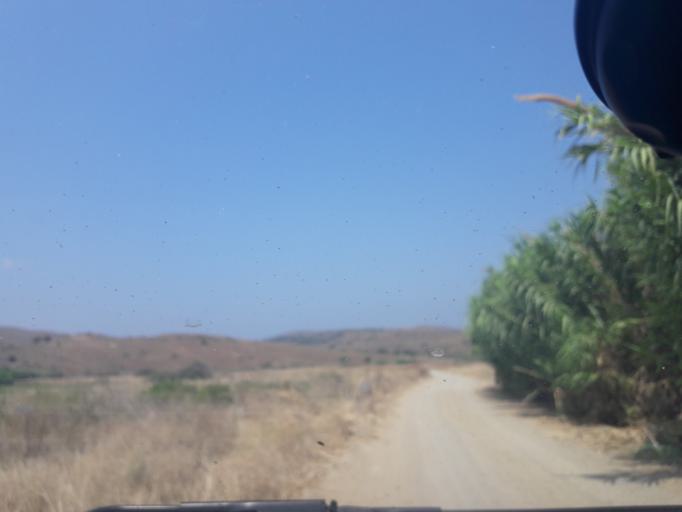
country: GR
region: North Aegean
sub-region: Nomos Lesvou
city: Myrina
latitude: 39.9796
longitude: 25.1498
